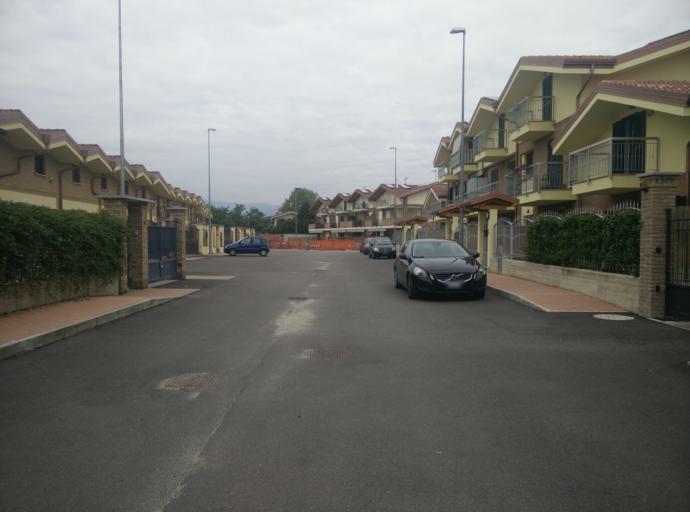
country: IT
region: Piedmont
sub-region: Provincia di Torino
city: Rivalta di Torino
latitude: 45.0225
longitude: 7.5210
